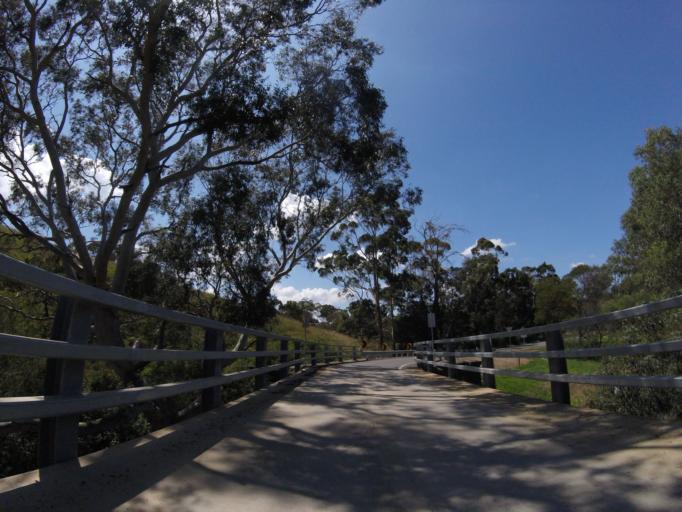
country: AU
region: Victoria
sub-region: Hume
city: Greenvale
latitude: -37.6094
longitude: 144.8018
